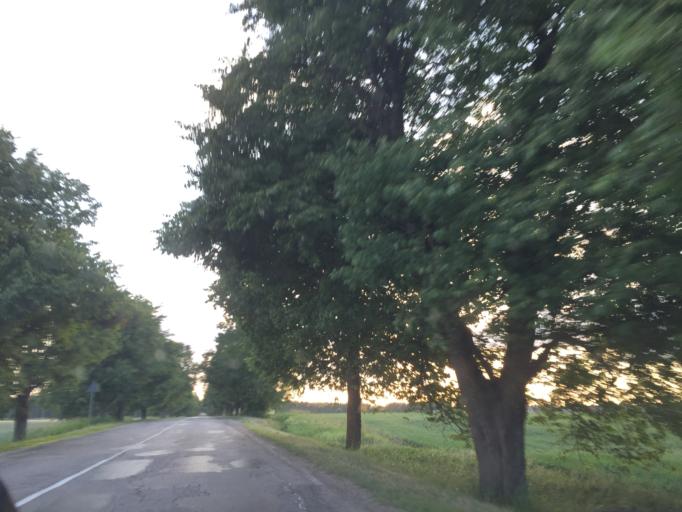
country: LV
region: Sigulda
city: Sigulda
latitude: 57.1375
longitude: 24.8926
